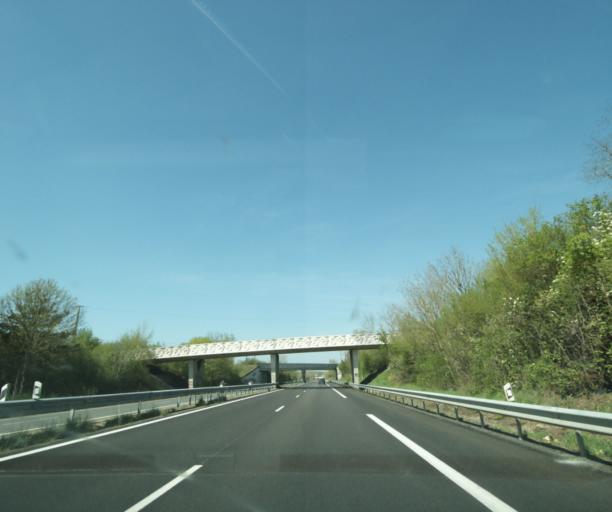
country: FR
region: Bourgogne
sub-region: Departement de la Nievre
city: La Charite-sur-Loire
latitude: 47.1966
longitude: 3.0232
